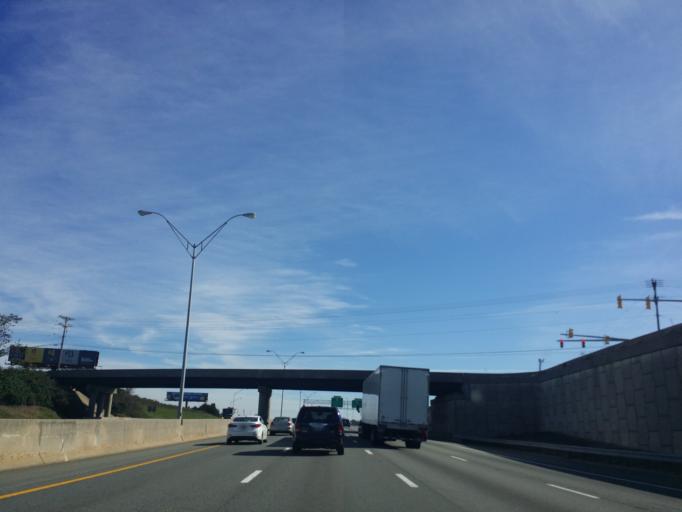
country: US
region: North Carolina
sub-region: Alamance County
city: Graham
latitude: 36.0609
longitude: -79.4068
